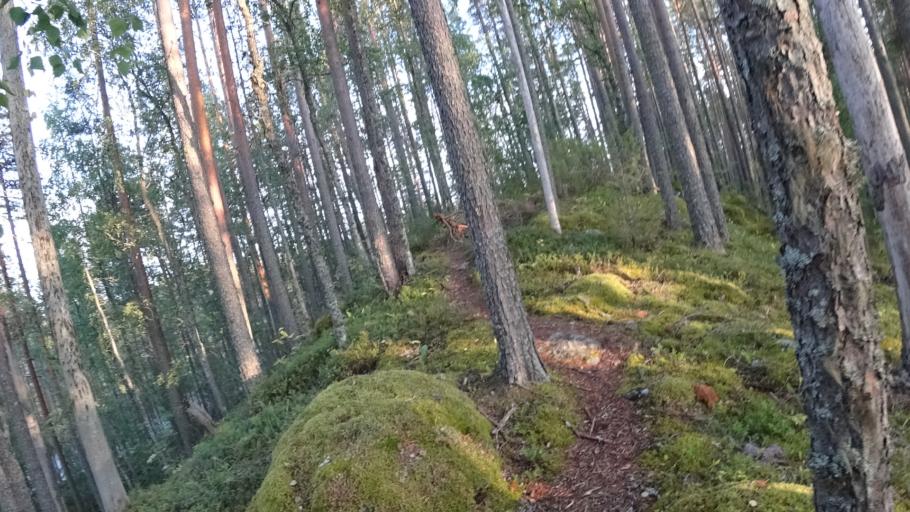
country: FI
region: North Karelia
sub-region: Joensuu
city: Ilomantsi
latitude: 62.5852
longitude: 31.1880
